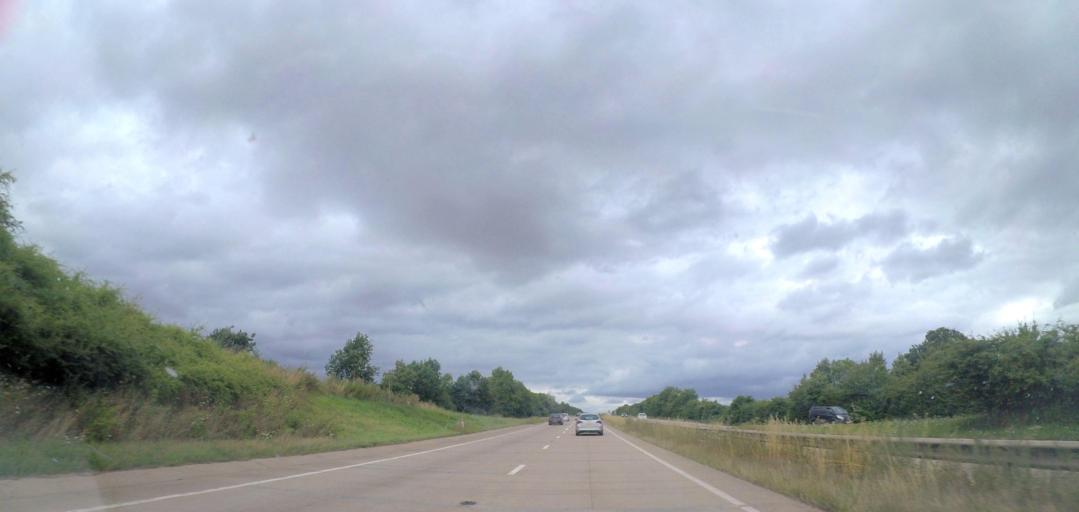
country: GB
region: England
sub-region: Norfolk
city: Hethersett
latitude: 52.5687
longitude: 1.1358
